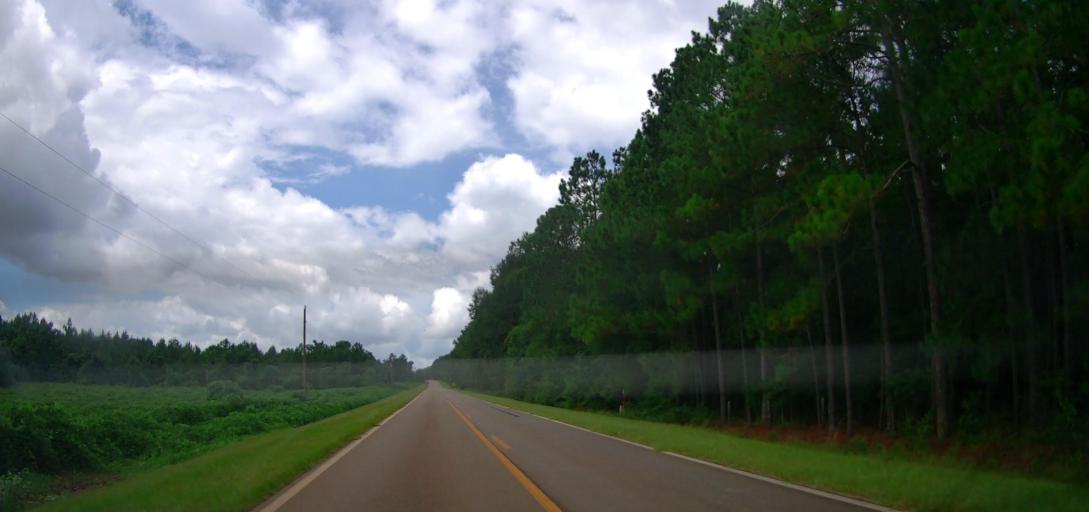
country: US
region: Georgia
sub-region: Pulaski County
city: Hawkinsville
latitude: 32.3386
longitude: -83.5454
